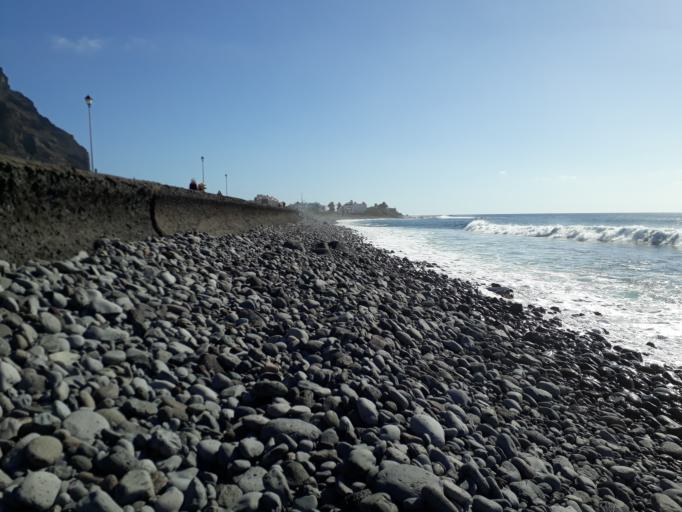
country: ES
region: Canary Islands
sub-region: Provincia de Santa Cruz de Tenerife
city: Alajero
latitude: 28.0927
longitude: -17.3406
